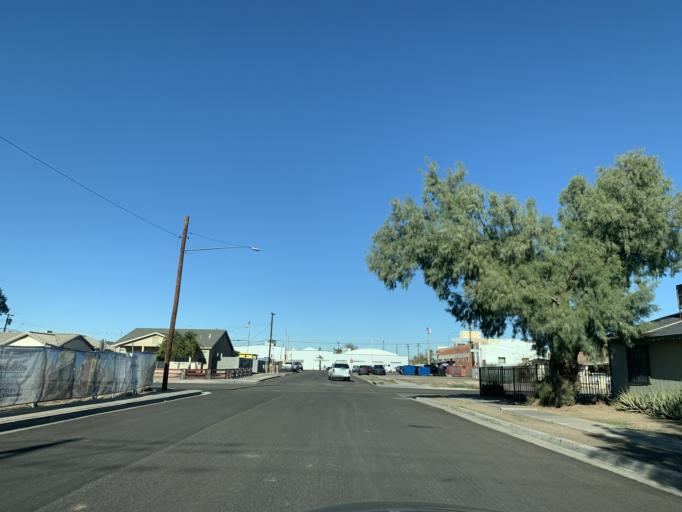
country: US
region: Arizona
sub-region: Maricopa County
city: Phoenix
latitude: 33.4501
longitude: -112.0499
